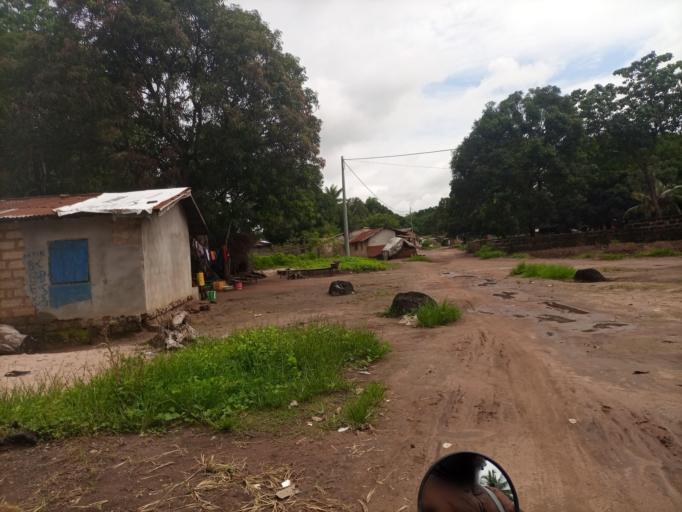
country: SL
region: Northern Province
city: Sawkta
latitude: 8.6280
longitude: -13.2027
